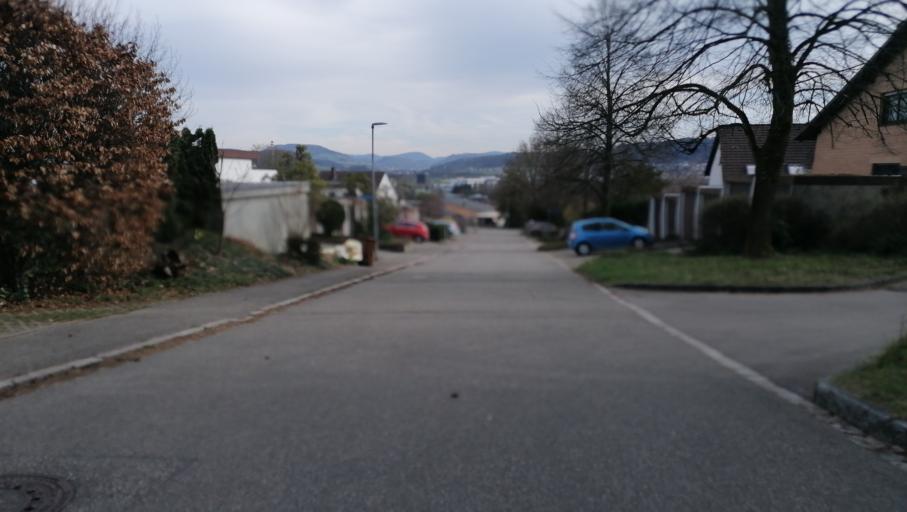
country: DE
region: Baden-Wuerttemberg
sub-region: Freiburg Region
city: Bad Sackingen
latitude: 47.5617
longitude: 7.9517
